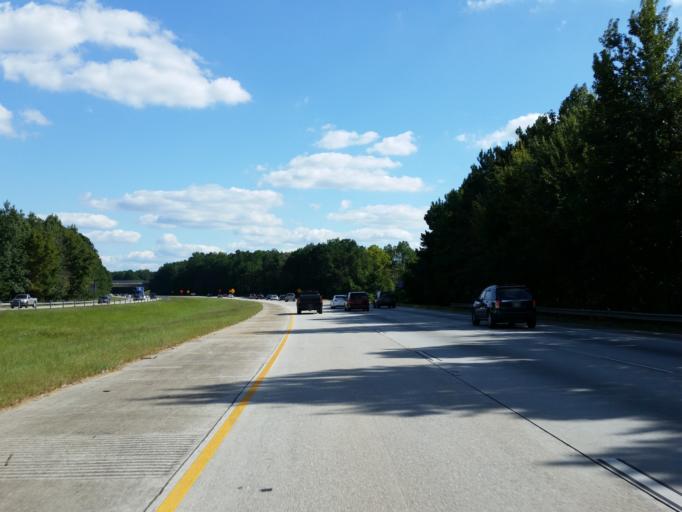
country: US
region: Georgia
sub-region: Clayton County
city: Lake City
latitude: 33.6037
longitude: -84.2948
